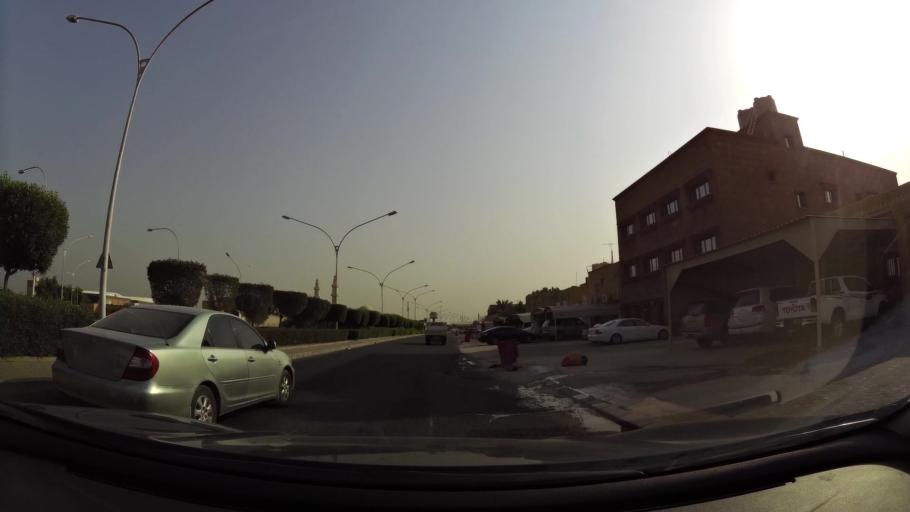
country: KW
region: Al Ahmadi
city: Al Manqaf
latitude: 29.1107
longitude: 48.1057
